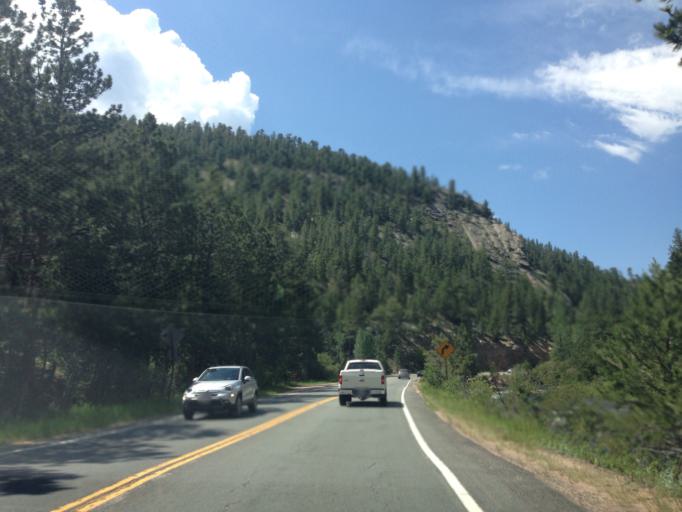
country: US
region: Colorado
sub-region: Larimer County
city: Estes Park
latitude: 40.3825
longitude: -105.4704
